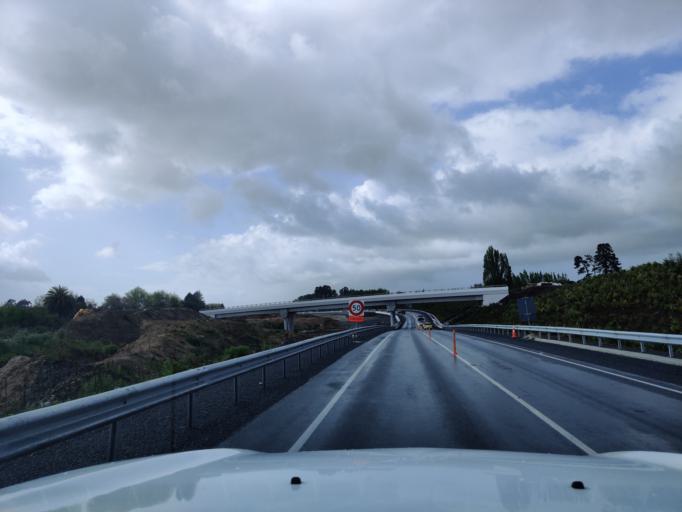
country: NZ
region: Waikato
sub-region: Hamilton City
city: Hamilton
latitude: -37.8152
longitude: 175.3418
